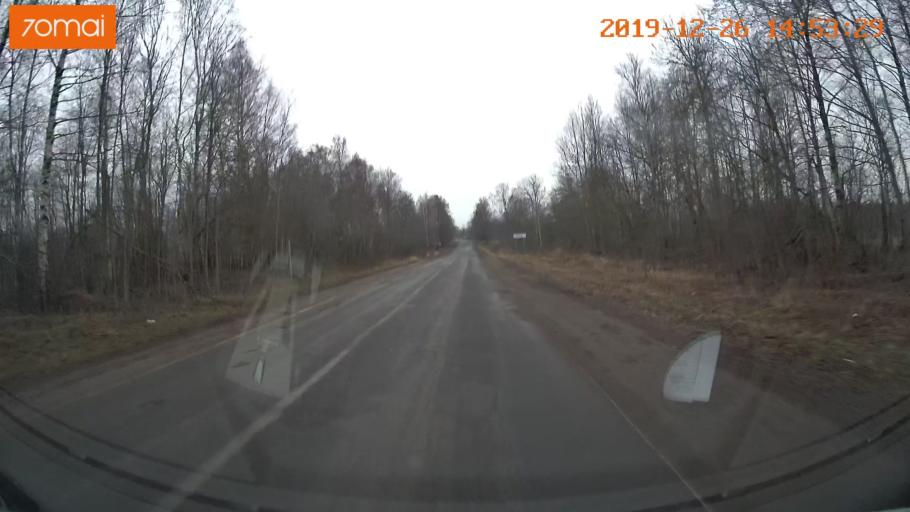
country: RU
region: Jaroslavl
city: Rybinsk
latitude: 58.3147
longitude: 38.8890
